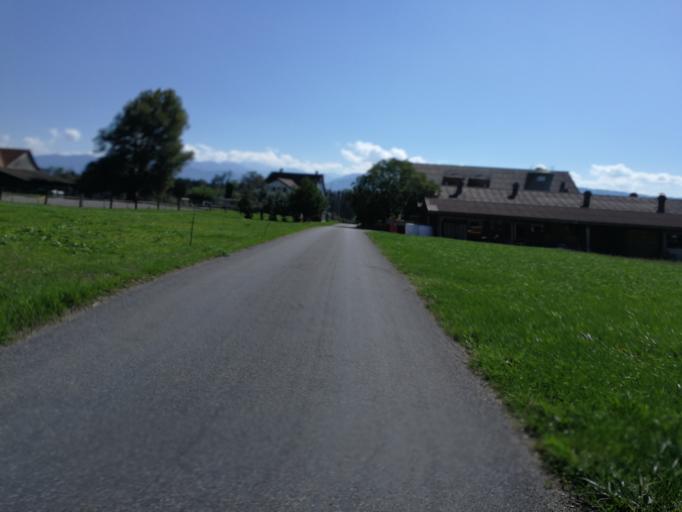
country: CH
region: Zurich
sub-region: Bezirk Hinwil
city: Durnten
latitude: 47.2682
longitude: 8.8353
